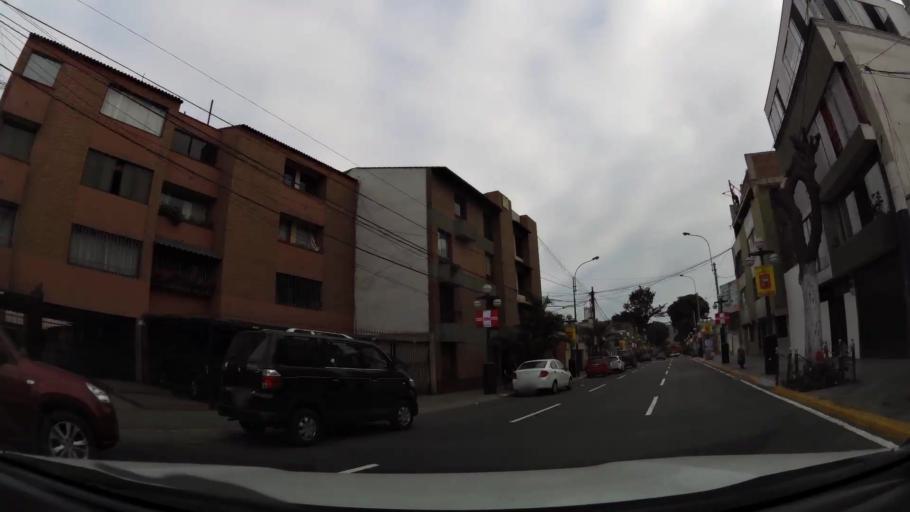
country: PE
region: Lima
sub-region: Lima
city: Surco
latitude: -12.1644
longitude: -77.0228
